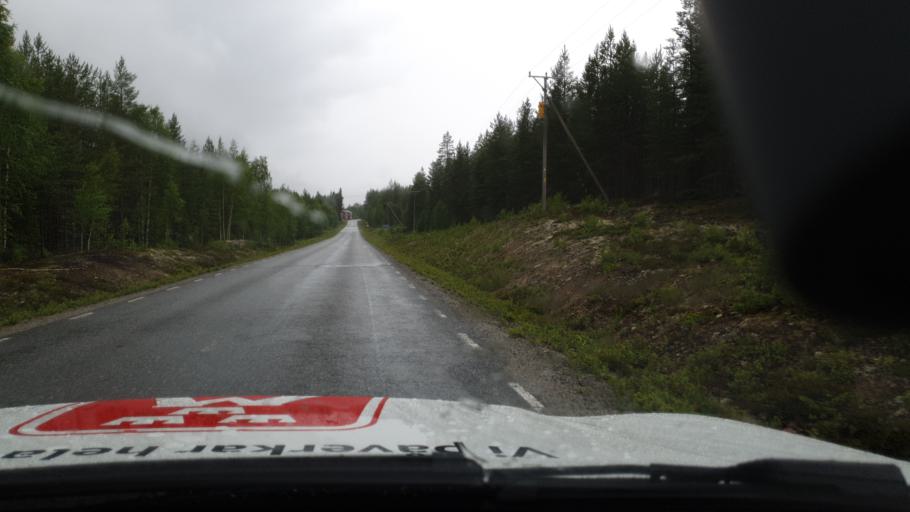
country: SE
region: Vaesterbotten
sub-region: Vindelns Kommun
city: Vindeln
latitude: 64.4022
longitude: 19.6606
